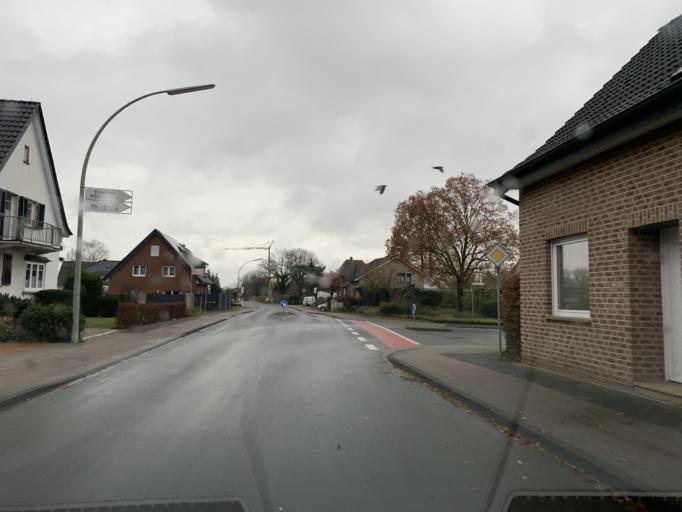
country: DE
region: North Rhine-Westphalia
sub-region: Regierungsbezirk Munster
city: Steinfurt
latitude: 52.1238
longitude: 7.4051
